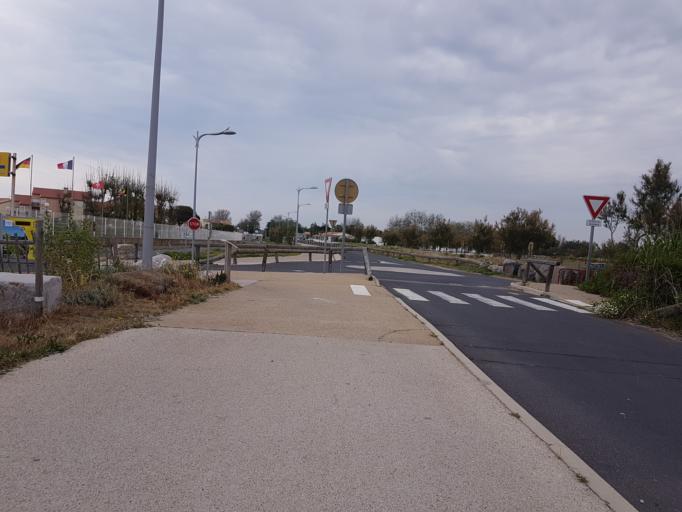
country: FR
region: Languedoc-Roussillon
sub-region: Departement de l'Herault
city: Marseillan
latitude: 43.3263
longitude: 3.5628
